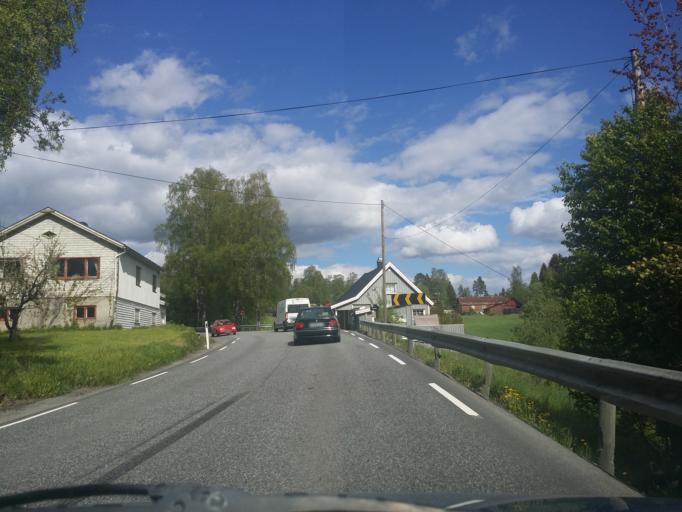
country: NO
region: Oppland
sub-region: Jevnaker
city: Jevnaker
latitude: 60.2660
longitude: 10.4885
